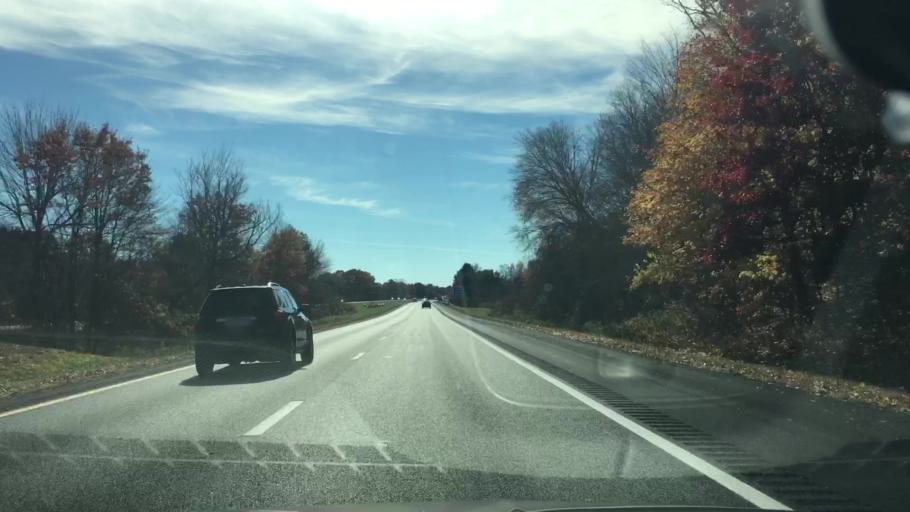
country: US
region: Massachusetts
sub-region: Hampshire County
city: Hatfield
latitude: 42.3748
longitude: -72.6330
